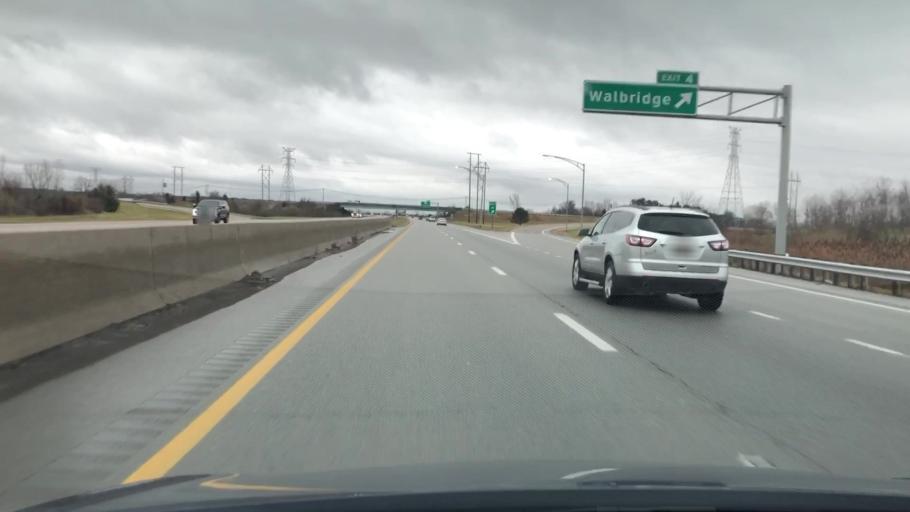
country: US
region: Ohio
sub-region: Wood County
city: Walbridge
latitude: 41.5917
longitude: -83.4769
